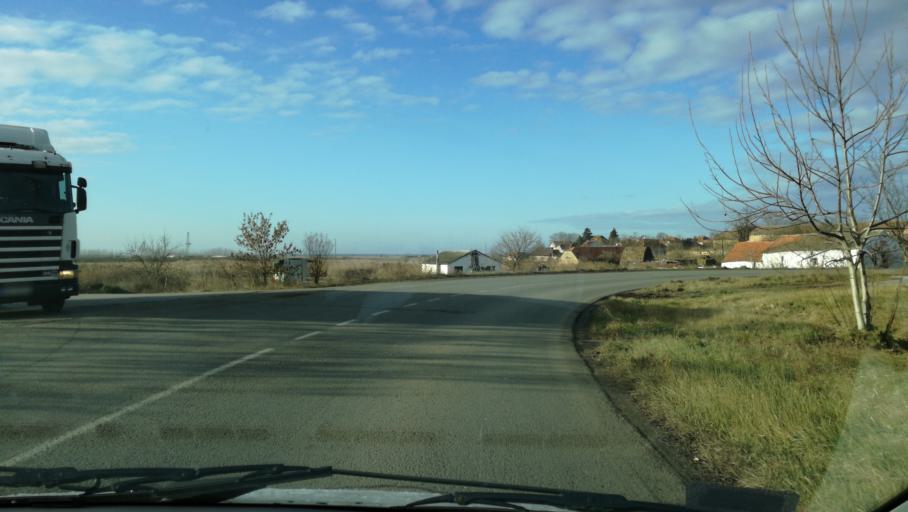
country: RS
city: Tiszahegyes
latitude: 45.8203
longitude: 20.3201
